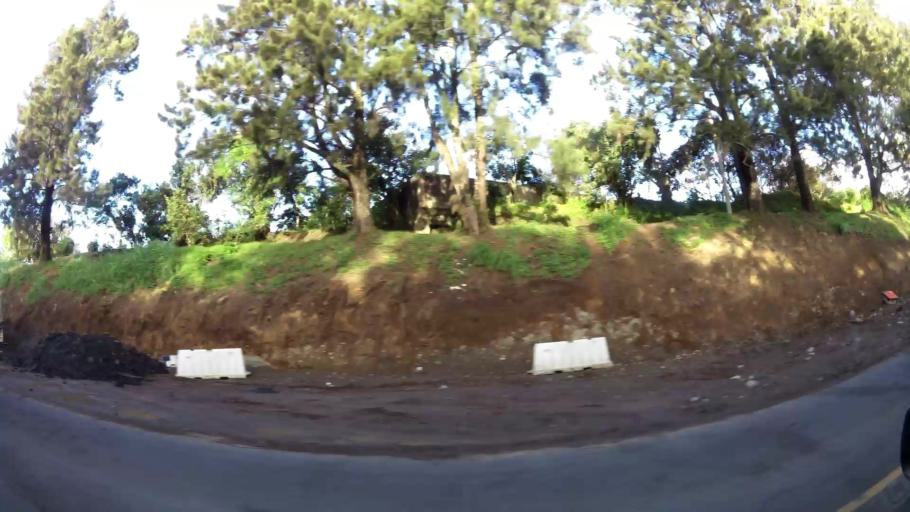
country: CR
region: Heredia
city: Angeles
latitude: 10.0112
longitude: -84.0304
